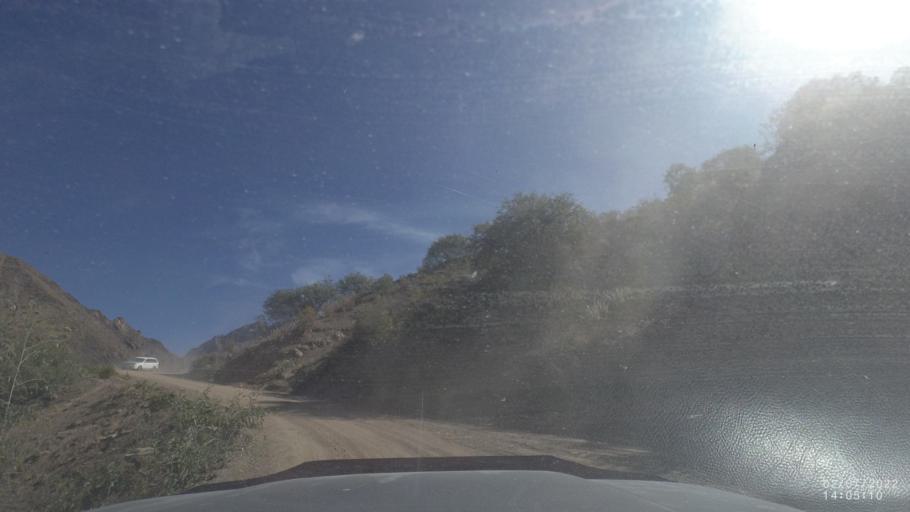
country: BO
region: Cochabamba
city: Irpa Irpa
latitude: -17.8211
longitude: -66.3960
